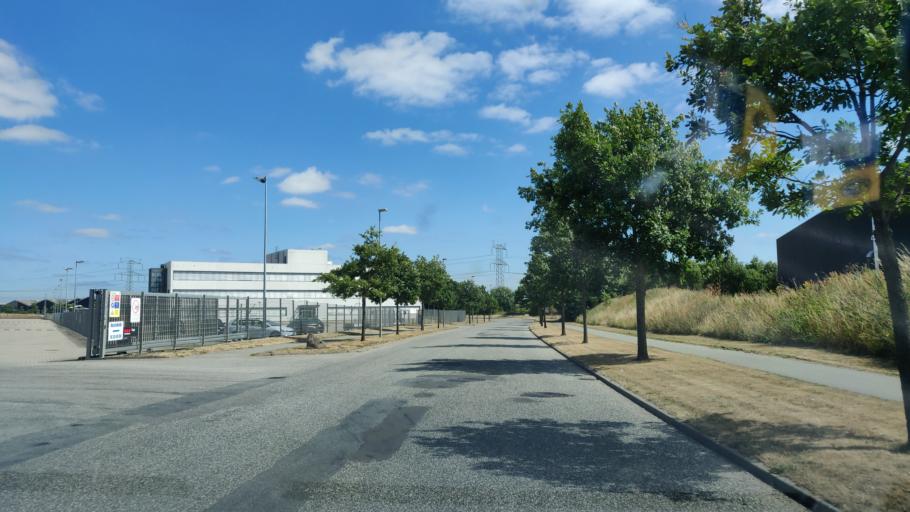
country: DK
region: South Denmark
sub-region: Kolding Kommune
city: Kolding
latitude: 55.5403
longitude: 9.4965
